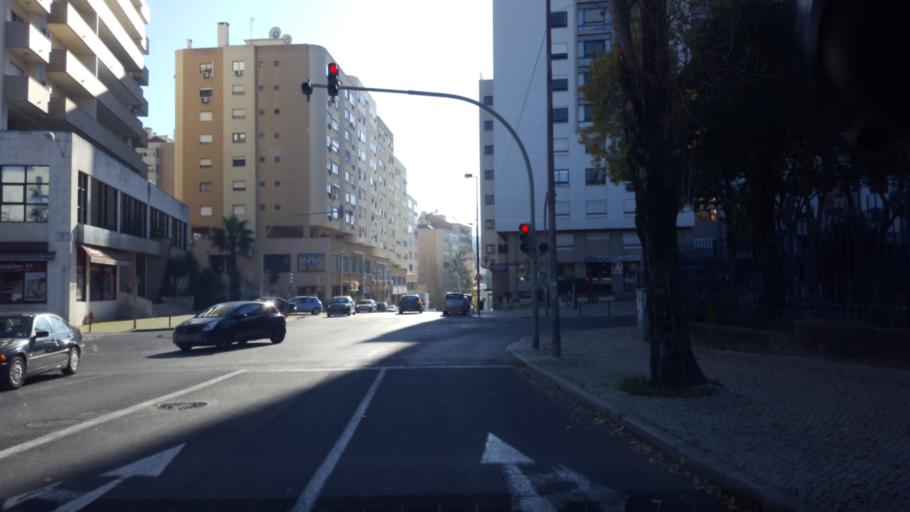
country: PT
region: Lisbon
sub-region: Odivelas
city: Pontinha
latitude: 38.7485
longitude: -9.1803
